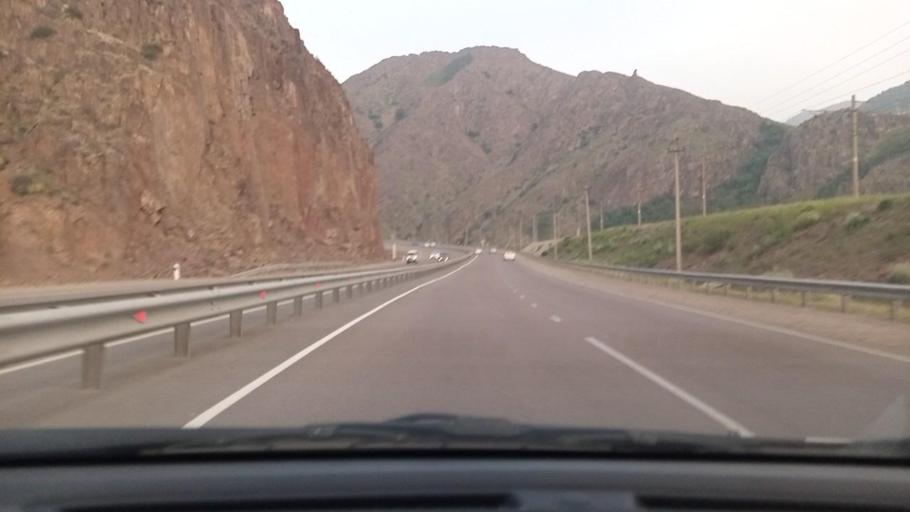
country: UZ
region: Toshkent
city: Angren
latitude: 41.0756
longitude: 70.3066
